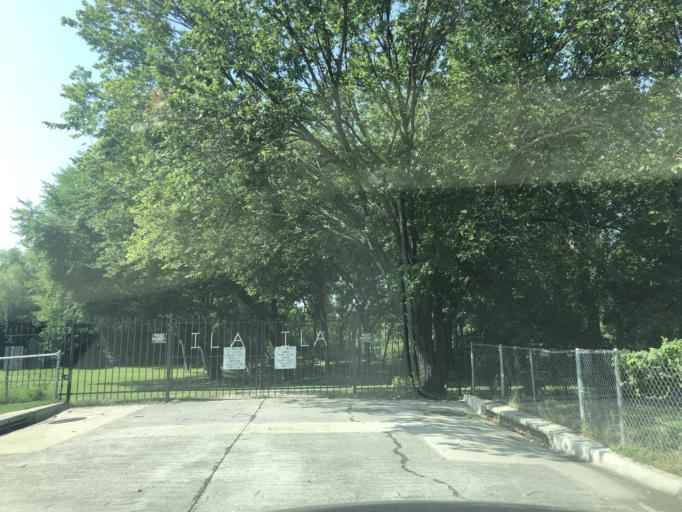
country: US
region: Texas
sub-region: Dallas County
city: Irving
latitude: 32.7966
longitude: -96.9647
